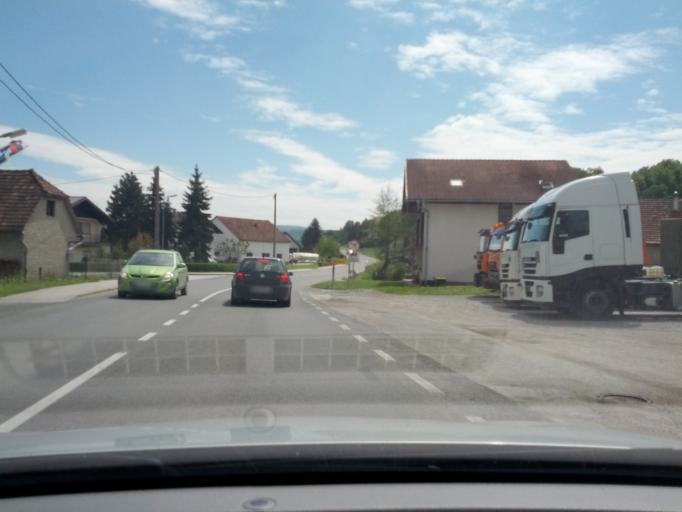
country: SI
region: Podcetrtek
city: Podcetrtek
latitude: 46.1314
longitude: 15.5988
